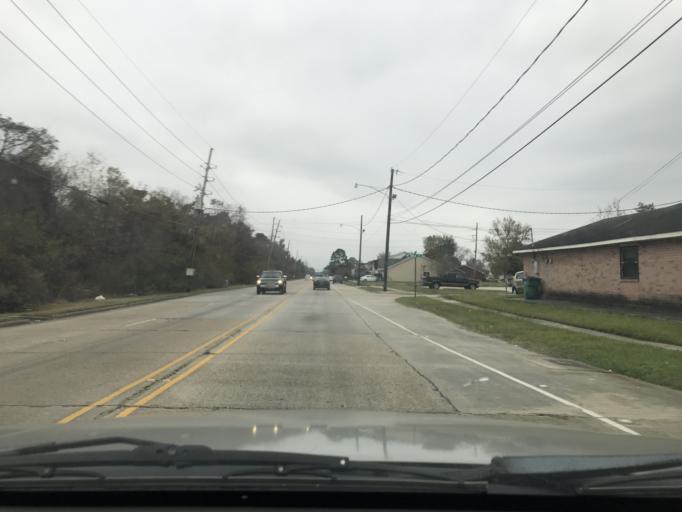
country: US
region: Louisiana
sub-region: Jefferson Parish
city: Woodmere
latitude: 29.8622
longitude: -90.0730
